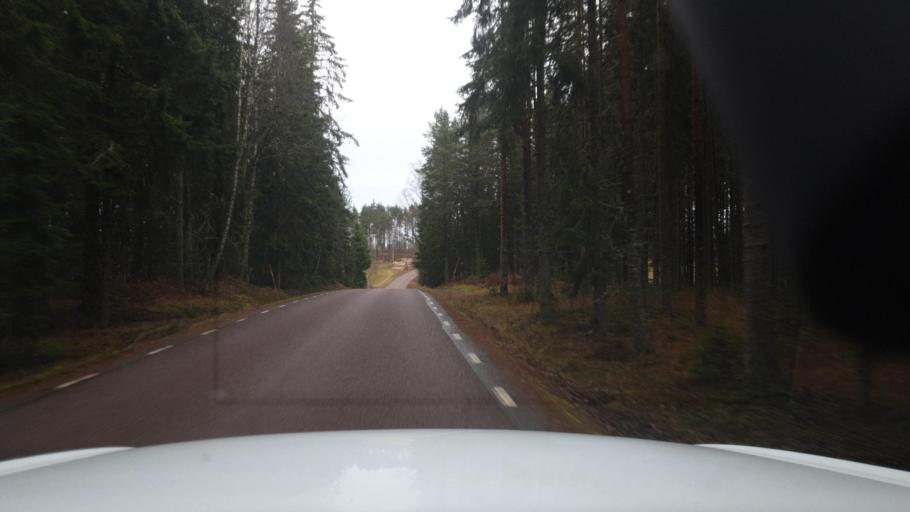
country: SE
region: Vaermland
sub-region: Karlstads Kommun
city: Edsvalla
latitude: 59.4819
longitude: 13.0810
